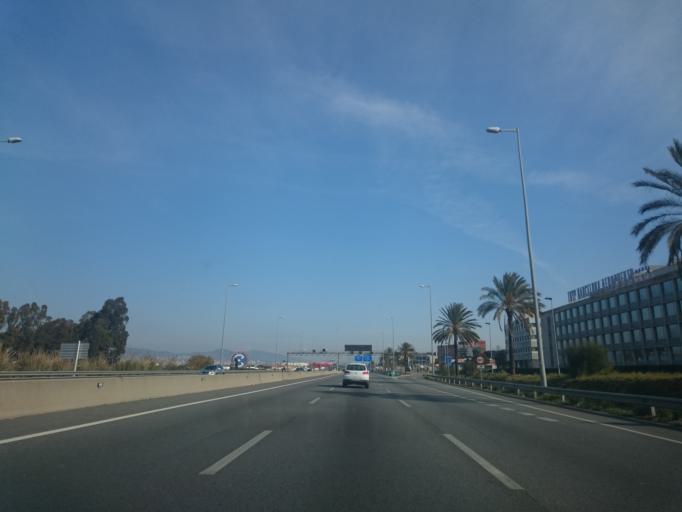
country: ES
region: Catalonia
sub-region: Provincia de Barcelona
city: El Prat de Llobregat
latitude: 41.3122
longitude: 2.0672
